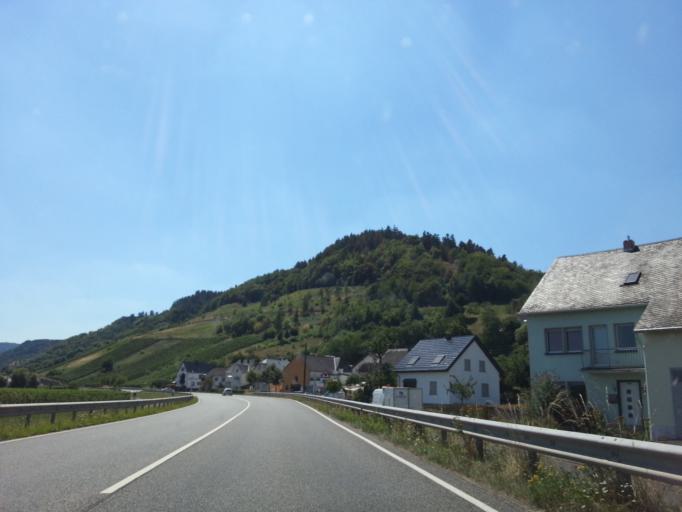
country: DE
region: Rheinland-Pfalz
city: Thornich
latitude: 49.8264
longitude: 6.8349
